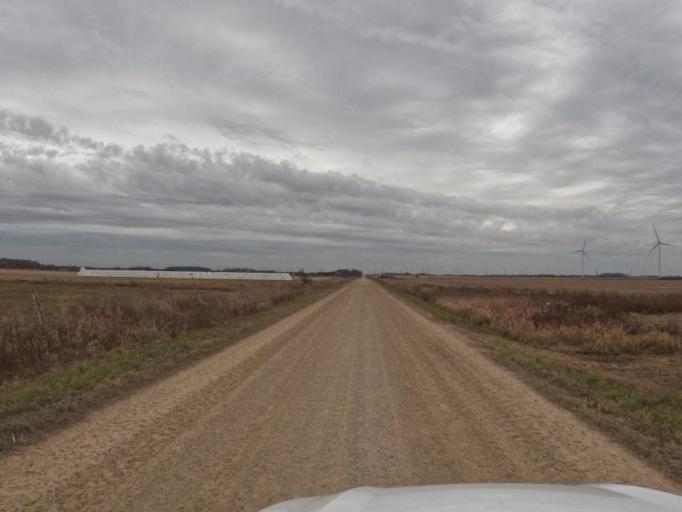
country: CA
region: Ontario
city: Shelburne
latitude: 44.0187
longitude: -80.3913
